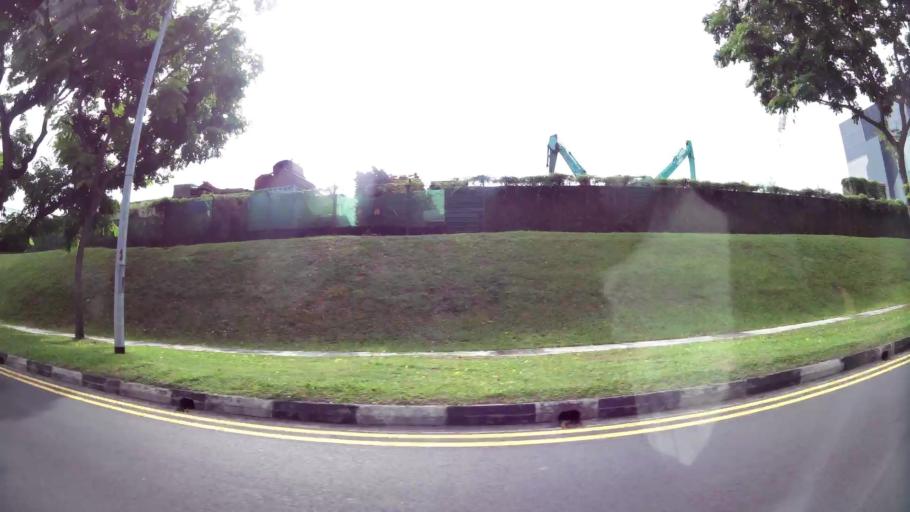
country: SG
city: Singapore
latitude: 1.3484
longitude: 103.8918
